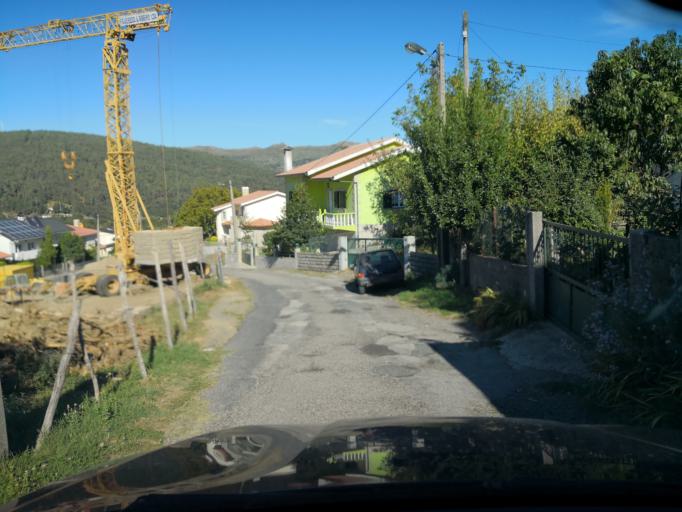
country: PT
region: Vila Real
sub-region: Santa Marta de Penaguiao
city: Santa Marta de Penaguiao
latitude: 41.2822
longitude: -7.8599
